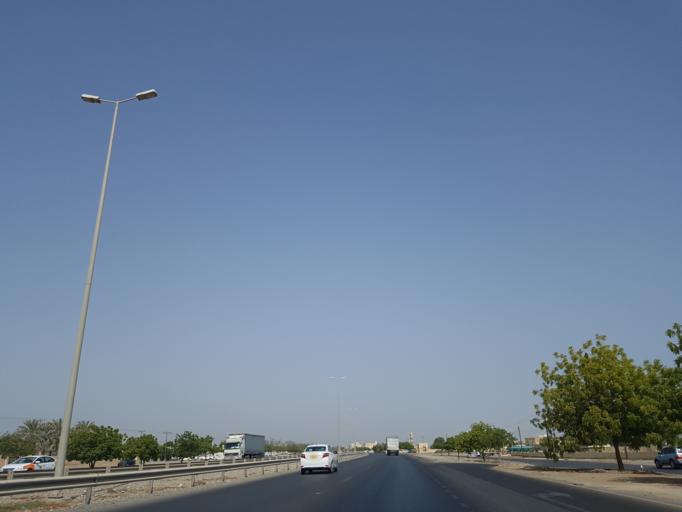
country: OM
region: Al Batinah
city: As Suwayq
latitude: 23.7542
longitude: 57.6076
